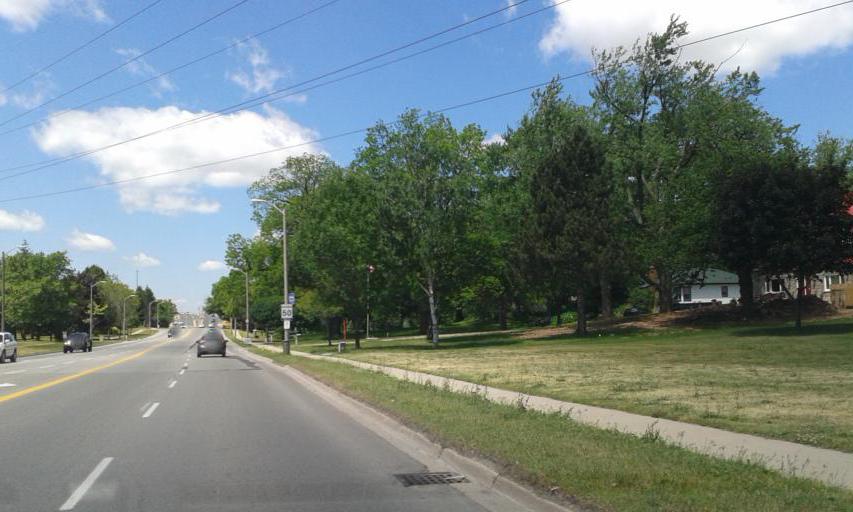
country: CA
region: Ontario
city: Niagara Falls
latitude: 43.1151
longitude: -79.1120
